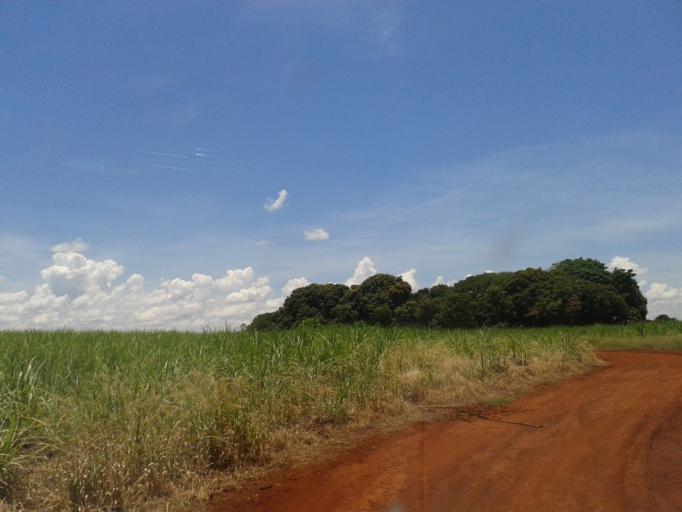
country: BR
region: Minas Gerais
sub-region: Centralina
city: Centralina
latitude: -18.6228
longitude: -49.2761
